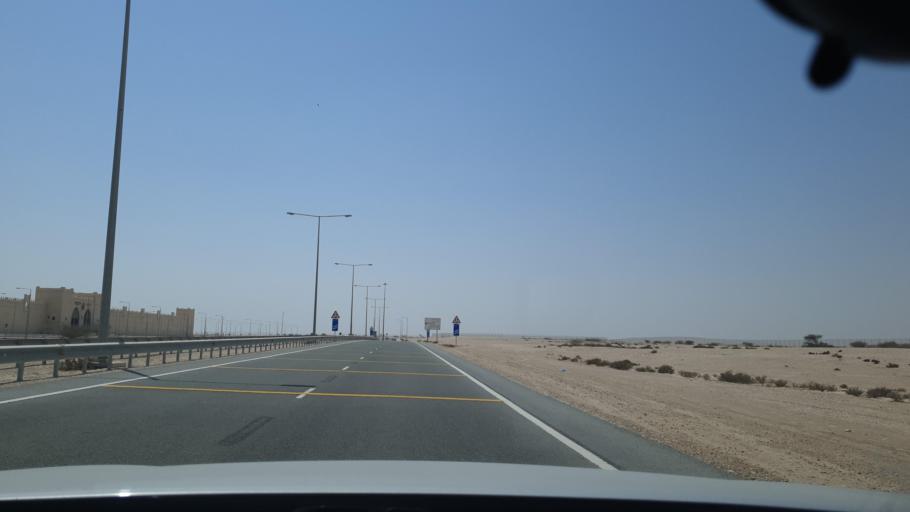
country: QA
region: Baladiyat ar Rayyan
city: Ar Rayyan
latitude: 25.3100
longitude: 51.3472
